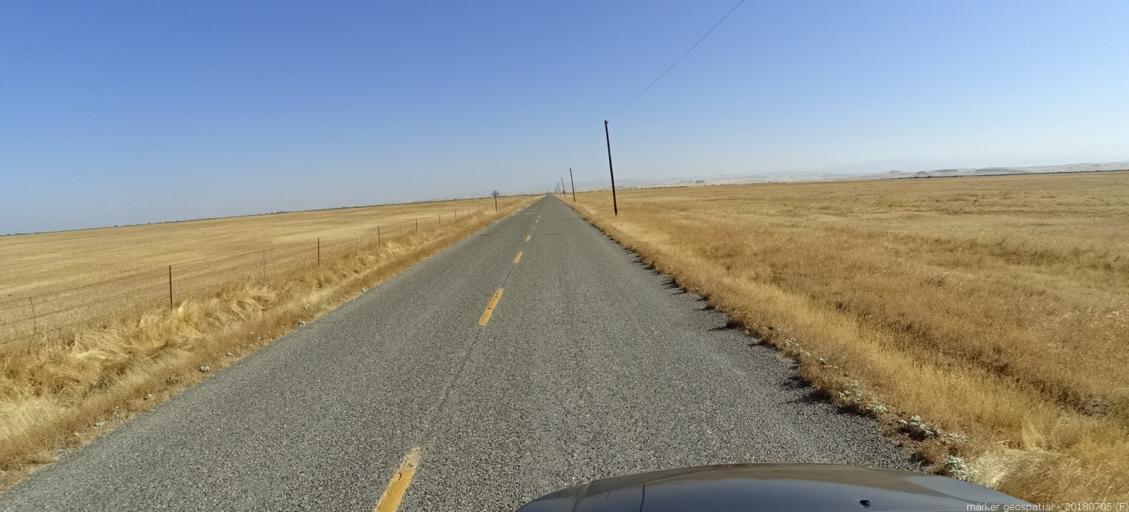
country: US
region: California
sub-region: Madera County
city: Madera Acres
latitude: 37.1279
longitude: -120.0746
